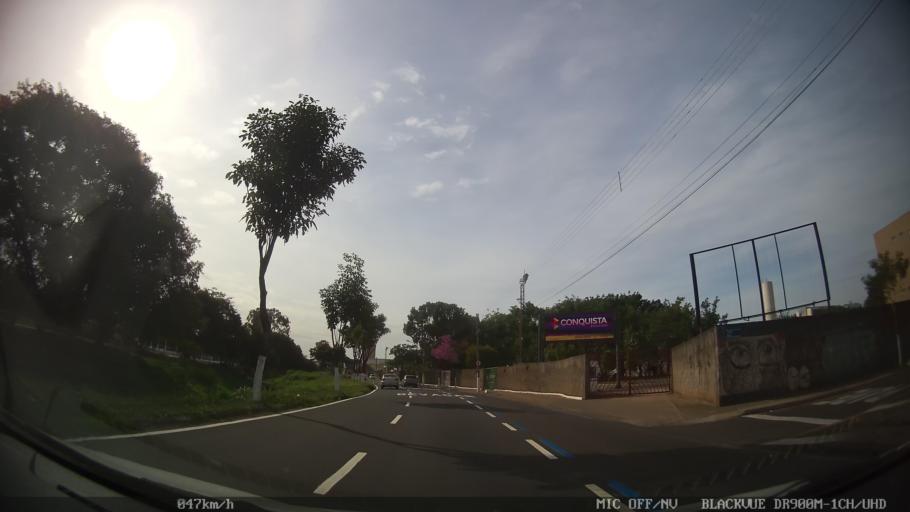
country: BR
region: Sao Paulo
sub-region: Piracicaba
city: Piracicaba
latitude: -22.7306
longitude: -47.6271
